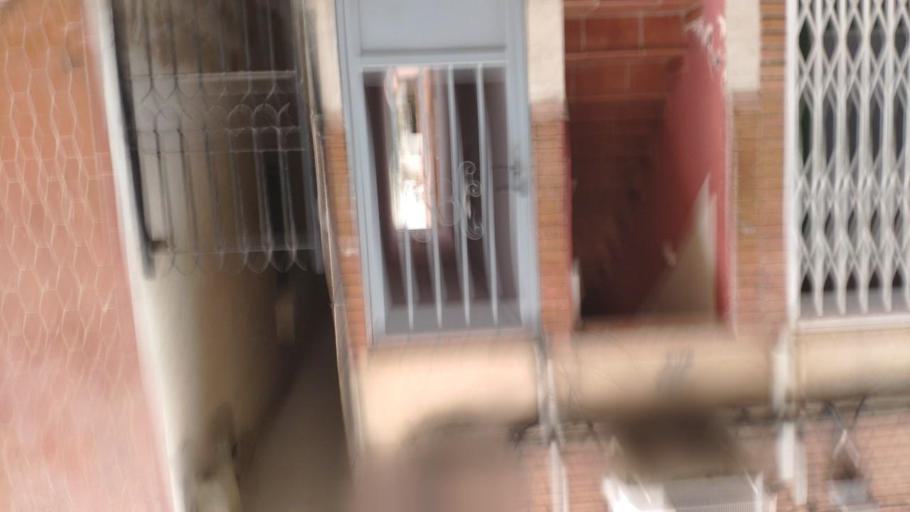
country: ES
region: Catalonia
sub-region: Provincia de Barcelona
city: Sant Cugat del Valles
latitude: 41.4730
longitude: 2.0893
